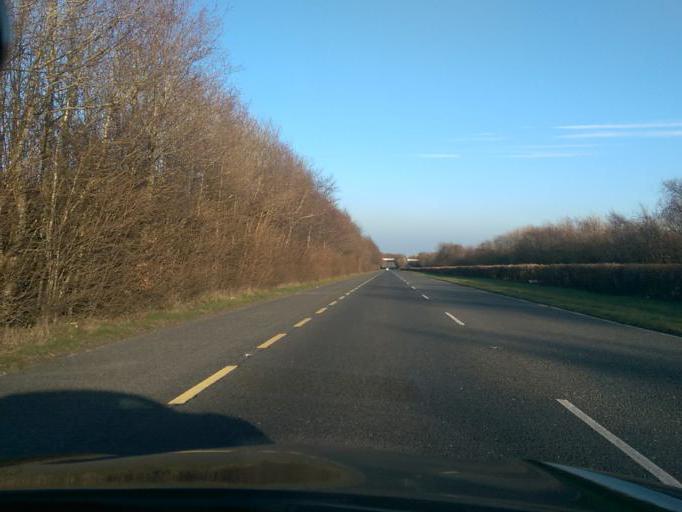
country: IE
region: Connaught
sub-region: County Galway
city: Oranmore
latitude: 53.2787
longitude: -8.9529
